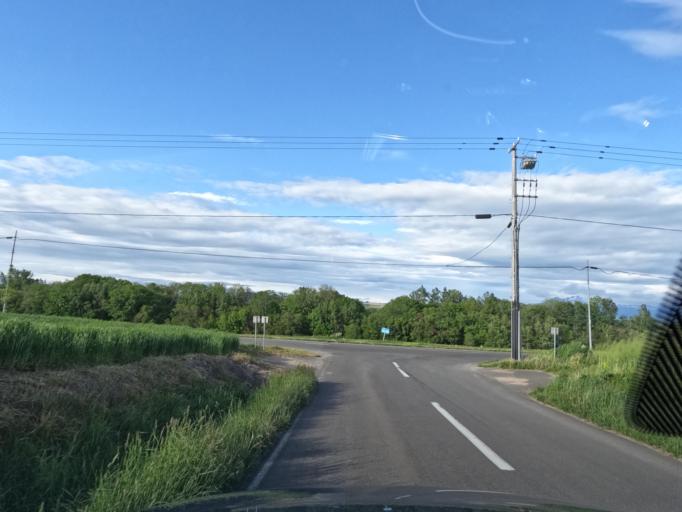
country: JP
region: Hokkaido
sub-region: Asahikawa-shi
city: Asahikawa
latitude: 43.6074
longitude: 142.4591
